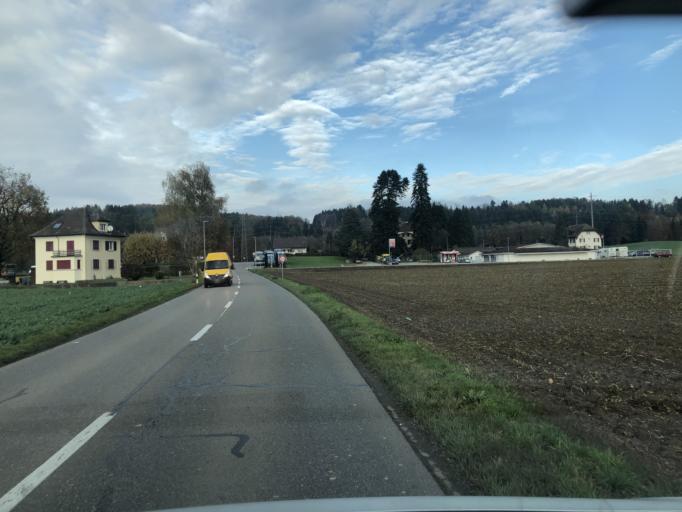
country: CH
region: Aargau
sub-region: Bezirk Baden
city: Mellingen
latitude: 47.4423
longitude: 8.2809
